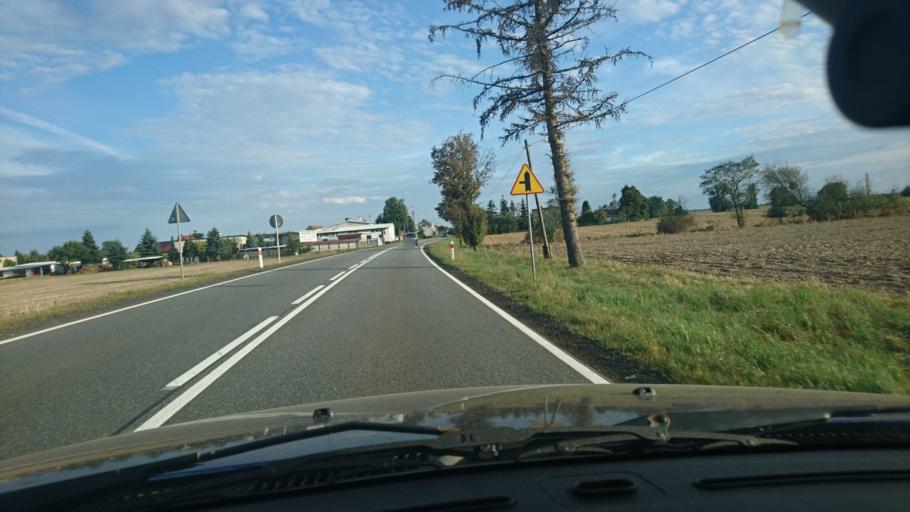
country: PL
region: Opole Voivodeship
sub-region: Powiat kluczborski
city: Kluczbork
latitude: 51.0102
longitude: 18.2039
